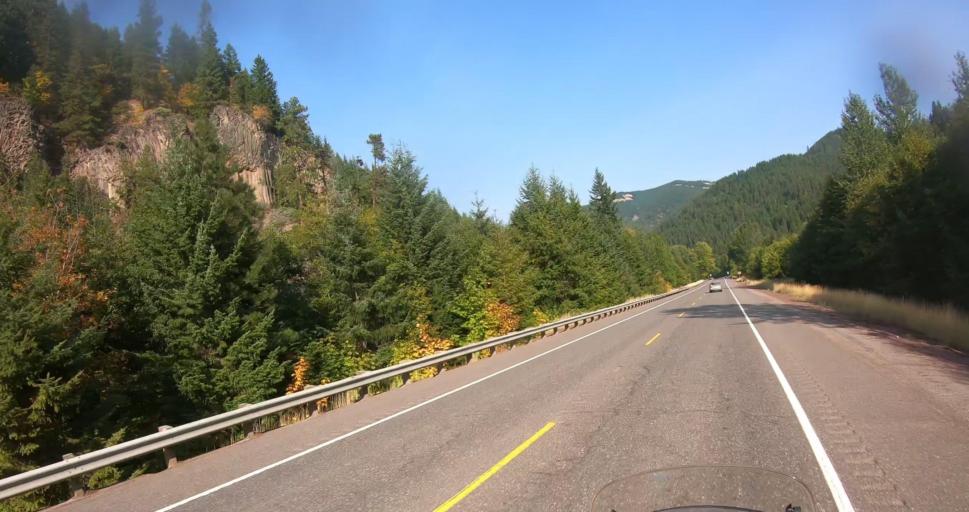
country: US
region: Oregon
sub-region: Hood River County
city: Odell
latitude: 45.4644
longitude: -121.5733
